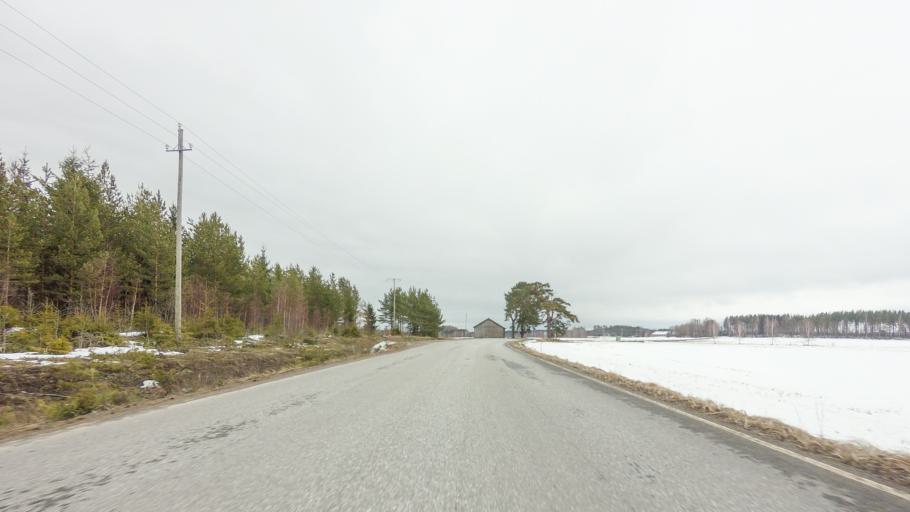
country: FI
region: Southern Savonia
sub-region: Savonlinna
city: Savonlinna
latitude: 61.9638
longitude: 28.8273
